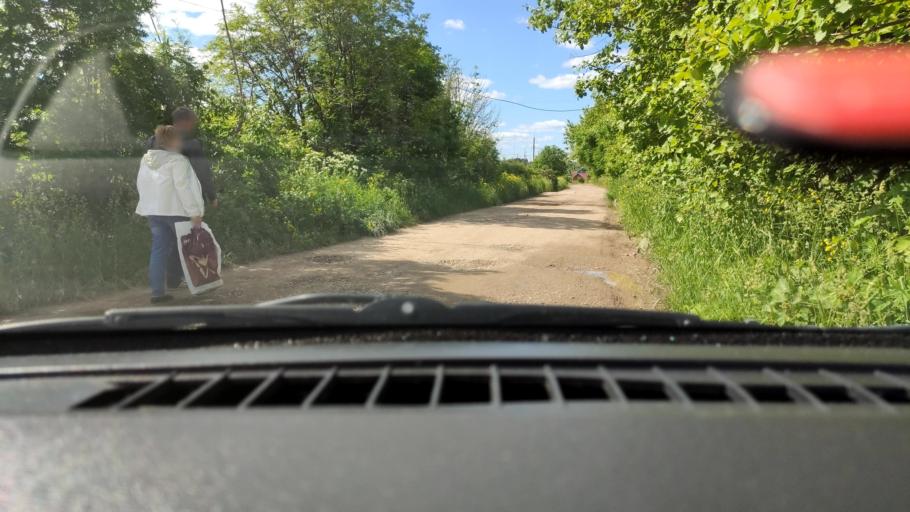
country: RU
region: Perm
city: Kultayevo
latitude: 57.8910
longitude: 55.9227
